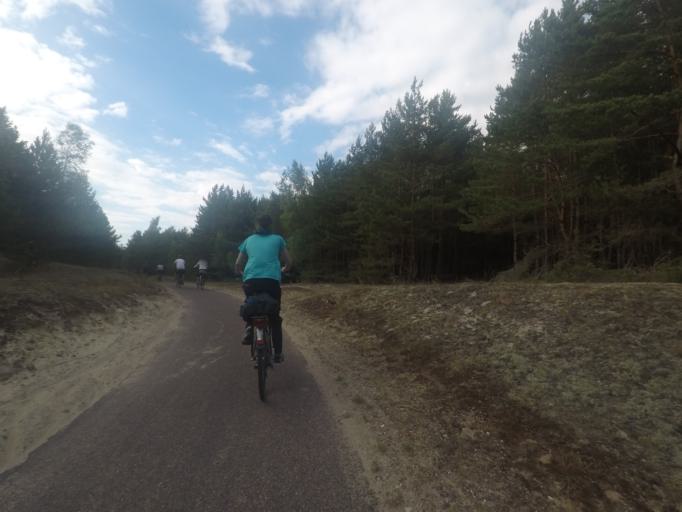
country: LT
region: Klaipedos apskritis
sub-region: Klaipeda
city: Klaipeda
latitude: 55.6268
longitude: 21.1199
